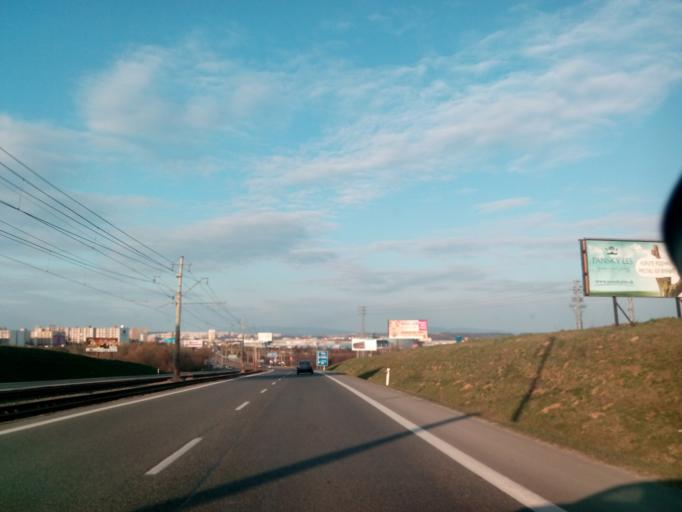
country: SK
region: Kosicky
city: Kosice
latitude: 48.6898
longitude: 21.2268
